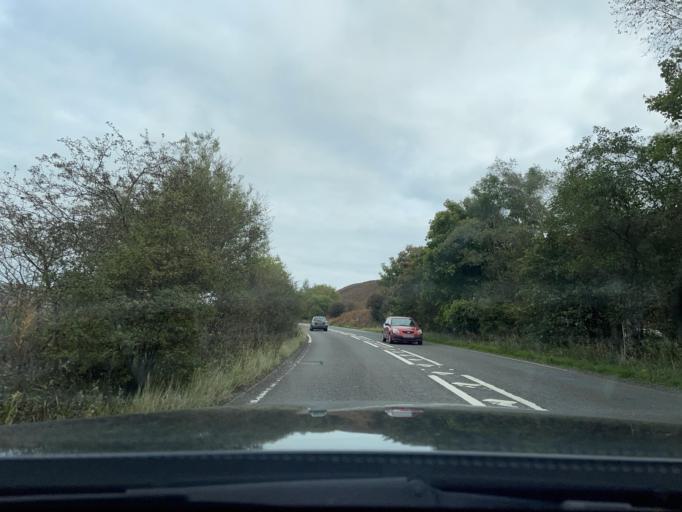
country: GB
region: England
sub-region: Derbyshire
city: Hathersage
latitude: 53.3834
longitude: -1.6757
